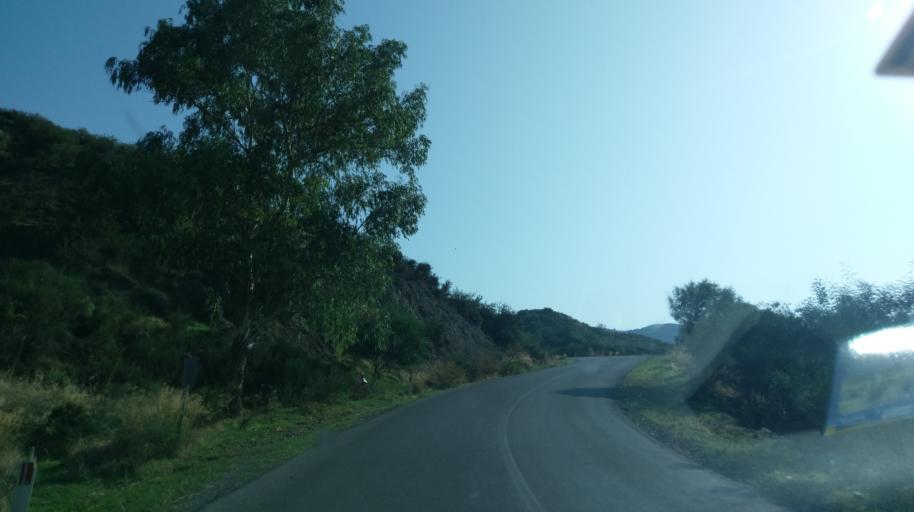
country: CY
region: Lefkosia
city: Kato Pyrgos
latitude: 35.1623
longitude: 32.7541
